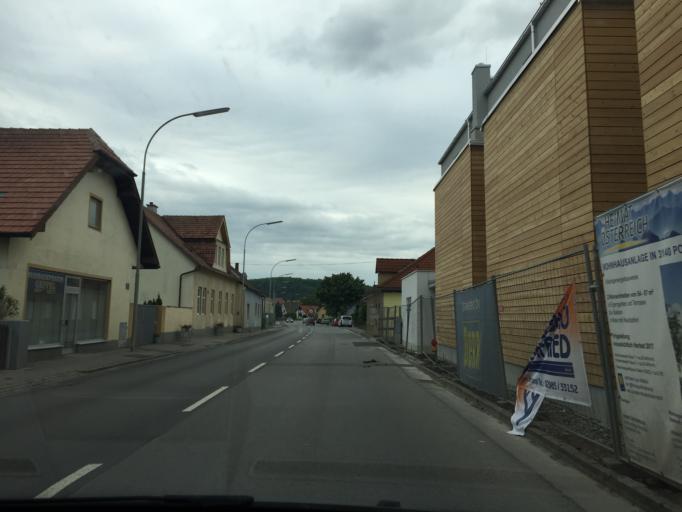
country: AT
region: Lower Austria
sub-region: Politischer Bezirk Sankt Polten
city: Herzogenburg
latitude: 48.2398
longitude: 15.6992
